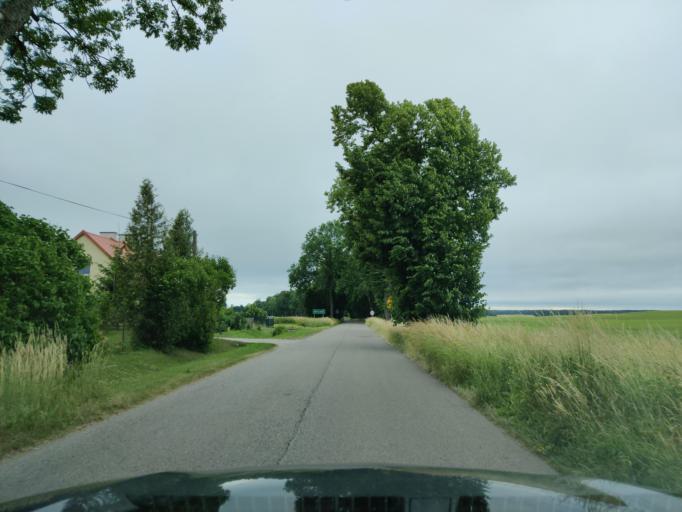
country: PL
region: Warmian-Masurian Voivodeship
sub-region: Powiat gizycki
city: Ryn
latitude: 53.9231
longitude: 21.5530
